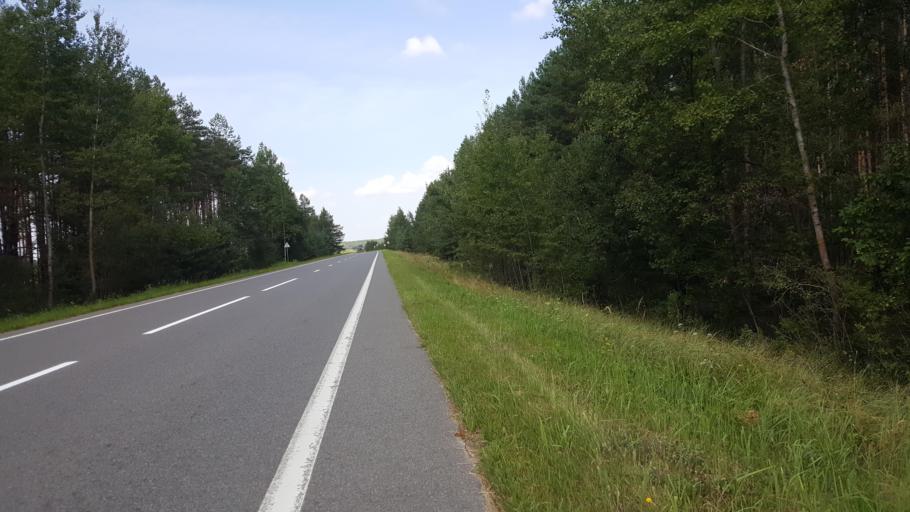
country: BY
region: Brest
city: Kamyanyuki
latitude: 52.5617
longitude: 23.6225
